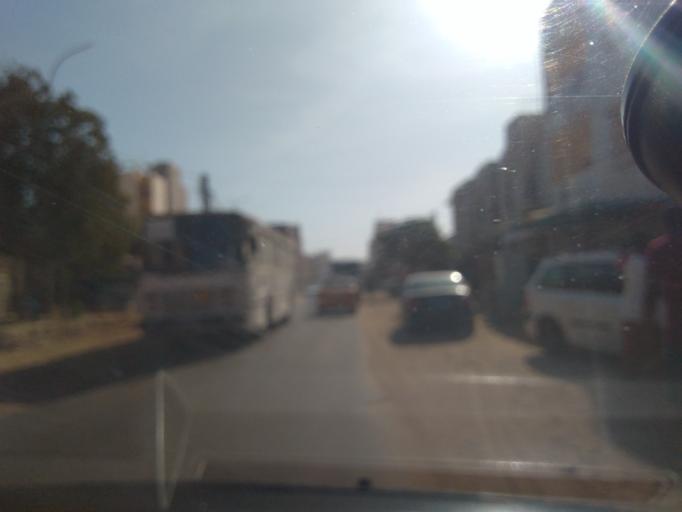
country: SN
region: Dakar
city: Grand Dakar
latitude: 14.7636
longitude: -17.4431
